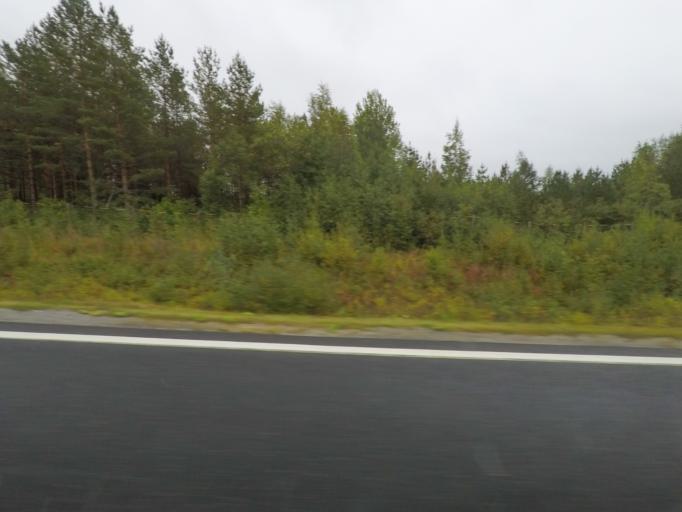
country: FI
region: Northern Savo
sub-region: Kuopio
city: Kuopio
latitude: 62.7137
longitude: 27.5740
